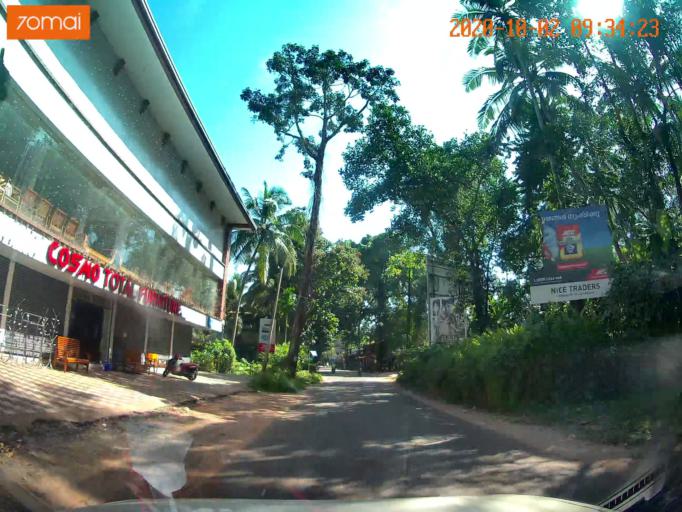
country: IN
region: Kerala
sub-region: Kozhikode
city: Nadapuram
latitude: 11.6375
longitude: 75.7538
